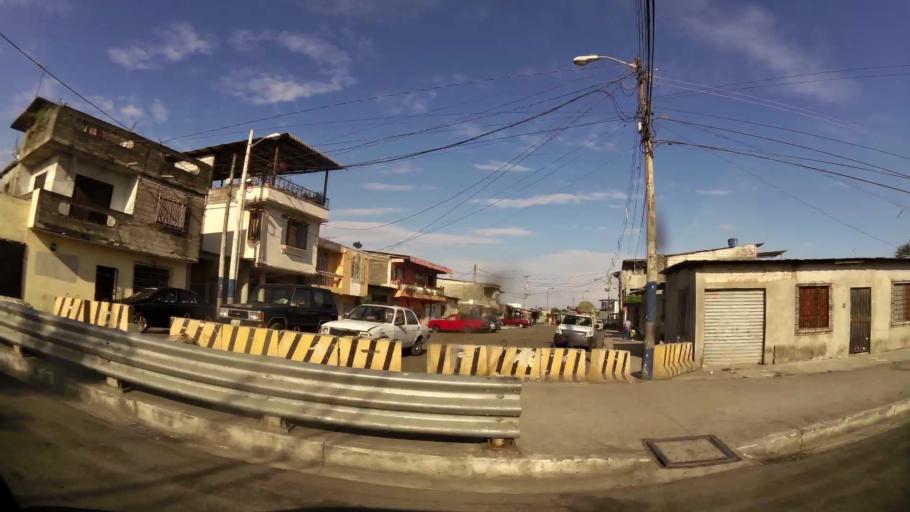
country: EC
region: Guayas
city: Guayaquil
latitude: -2.2193
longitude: -79.9167
